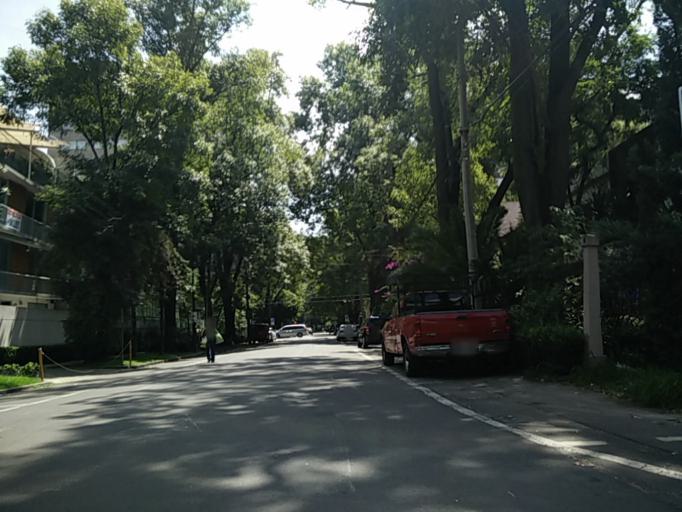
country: MX
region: Mexico City
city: Miguel Hidalgo
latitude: 19.4304
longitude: -99.1889
